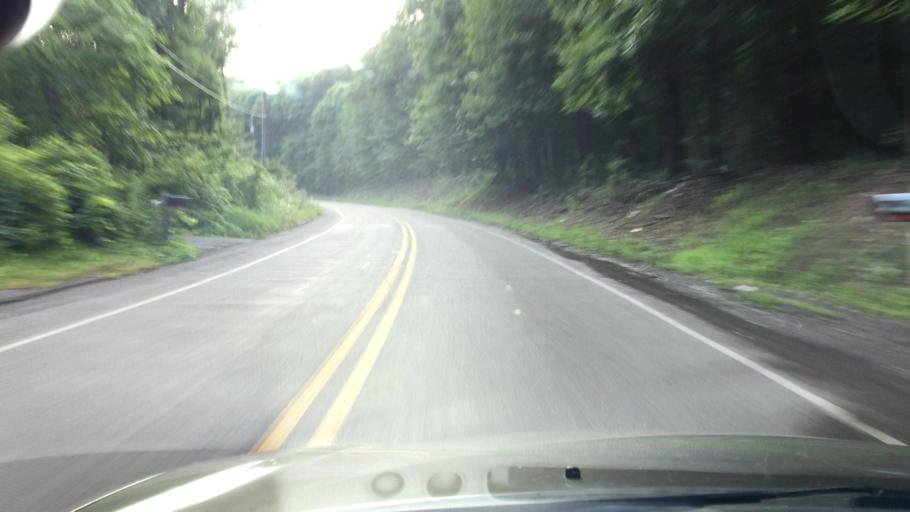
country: US
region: Pennsylvania
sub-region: Carbon County
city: Weatherly
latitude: 40.9279
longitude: -75.8760
